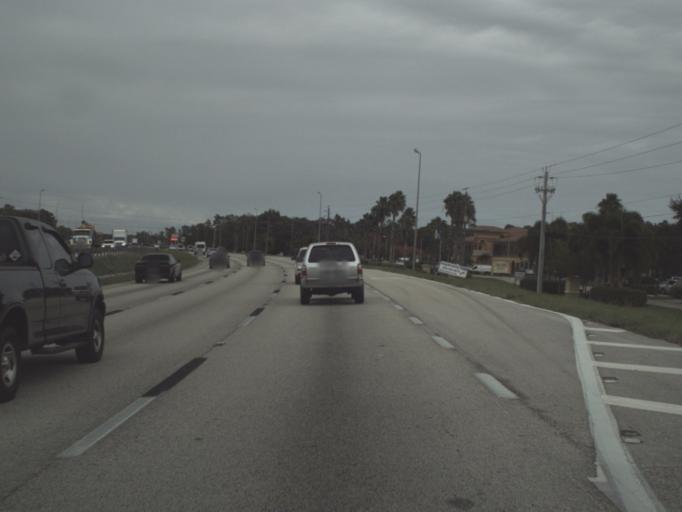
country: US
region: Florida
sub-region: Lee County
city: Fort Myers
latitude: 26.5984
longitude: -81.8347
